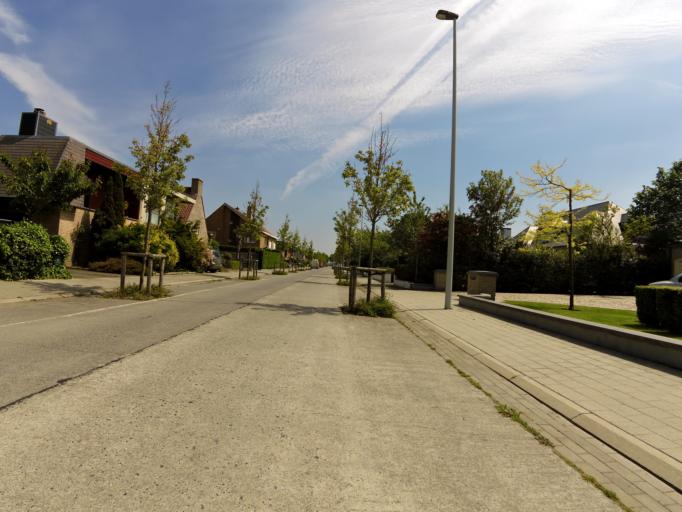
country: BE
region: Flanders
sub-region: Provincie West-Vlaanderen
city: Ostend
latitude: 51.2073
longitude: 2.8840
